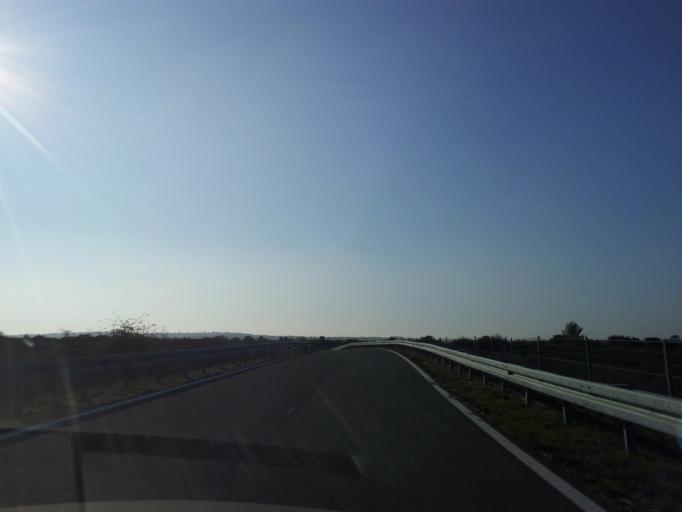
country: HR
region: Zadarska
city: Sukosan
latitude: 44.0720
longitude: 15.3411
